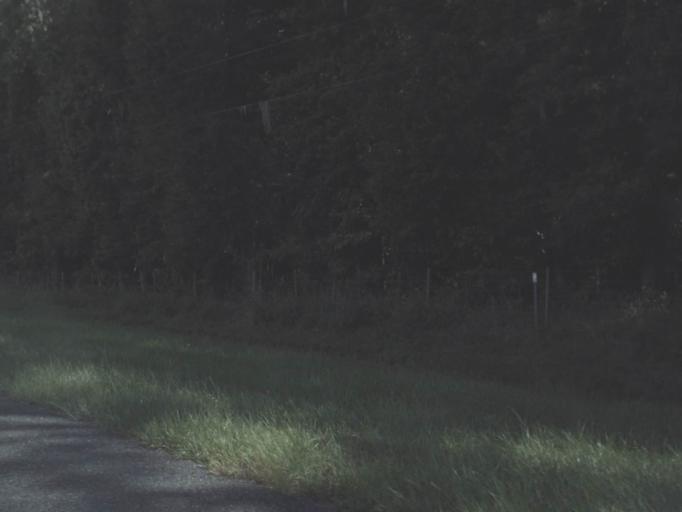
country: US
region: Florida
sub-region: Levy County
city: Chiefland
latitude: 29.4398
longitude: -82.8375
